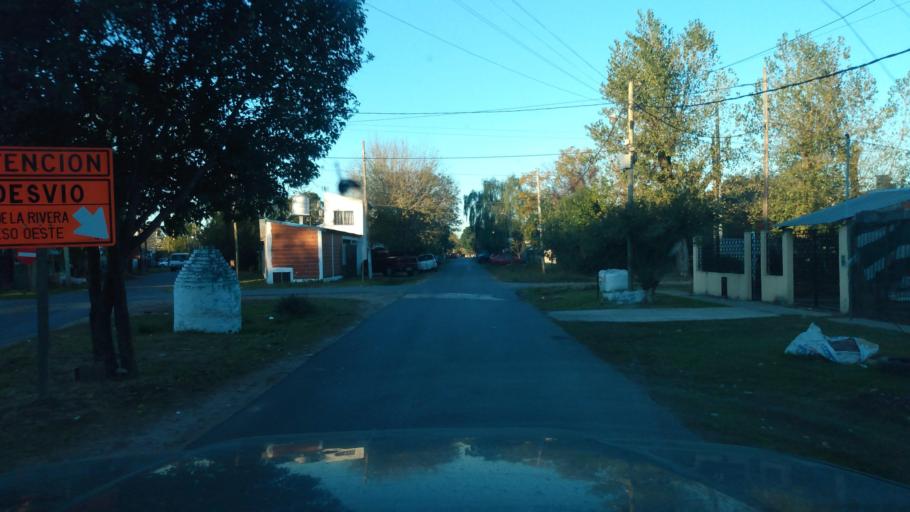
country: AR
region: Buenos Aires
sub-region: Partido de Merlo
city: Merlo
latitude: -34.6575
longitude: -58.7491
